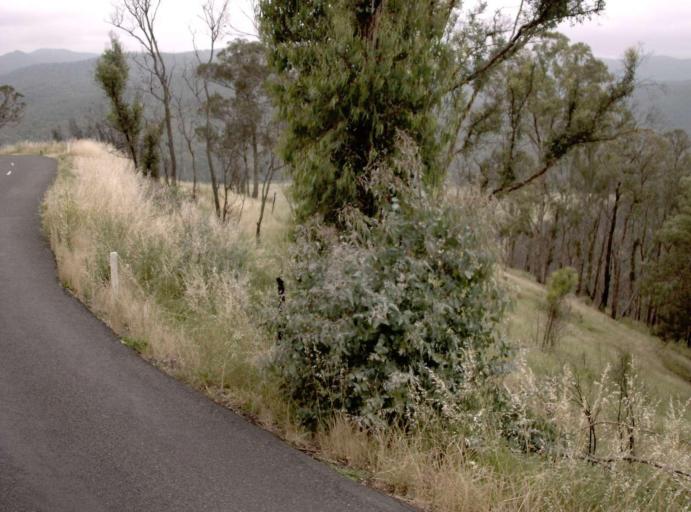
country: AU
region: Victoria
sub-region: Wellington
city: Heyfield
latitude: -37.8231
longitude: 146.6753
